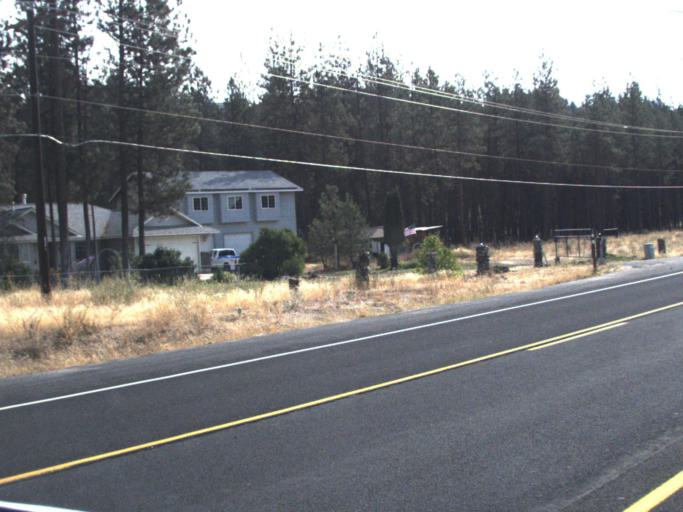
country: US
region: Washington
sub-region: Spokane County
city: Town and Country
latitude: 47.7501
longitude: -117.5098
